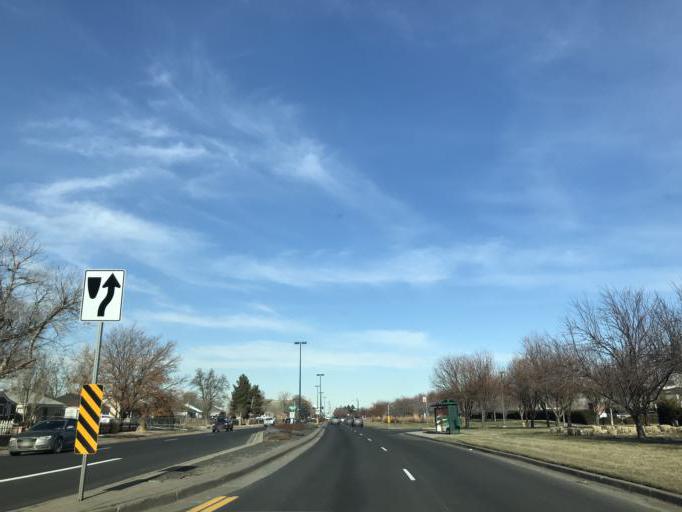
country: US
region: Colorado
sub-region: Arapahoe County
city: Glendale
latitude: 39.7552
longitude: -104.9034
